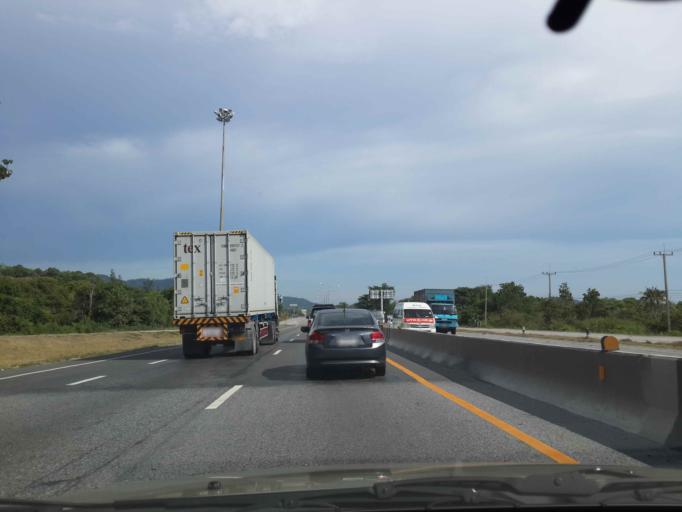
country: TH
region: Chon Buri
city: Chon Buri
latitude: 13.3293
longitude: 100.9897
